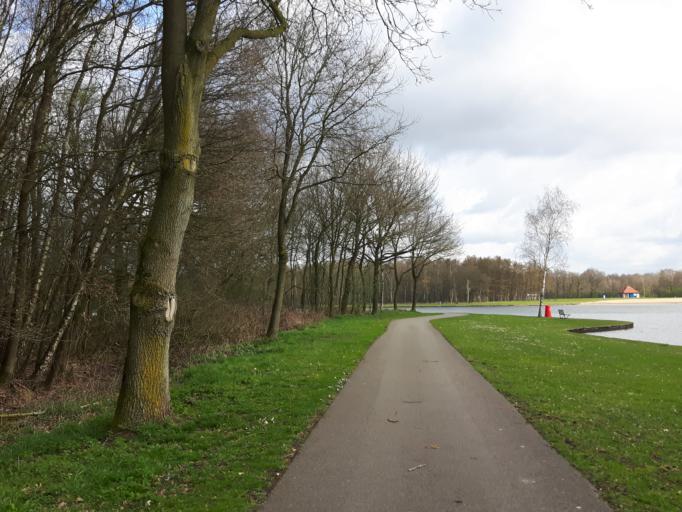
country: NL
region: Overijssel
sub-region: Gemeente Enschede
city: Enschede
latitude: 52.1773
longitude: 6.8336
